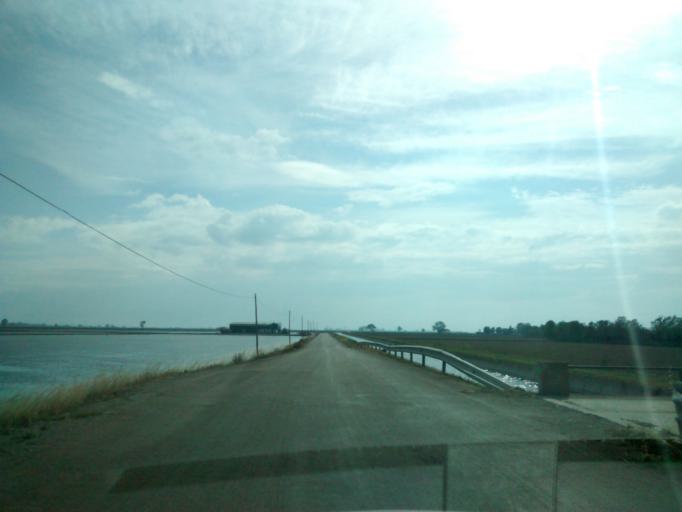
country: ES
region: Catalonia
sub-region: Provincia de Tarragona
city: Deltebre
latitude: 40.6967
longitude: 0.8067
